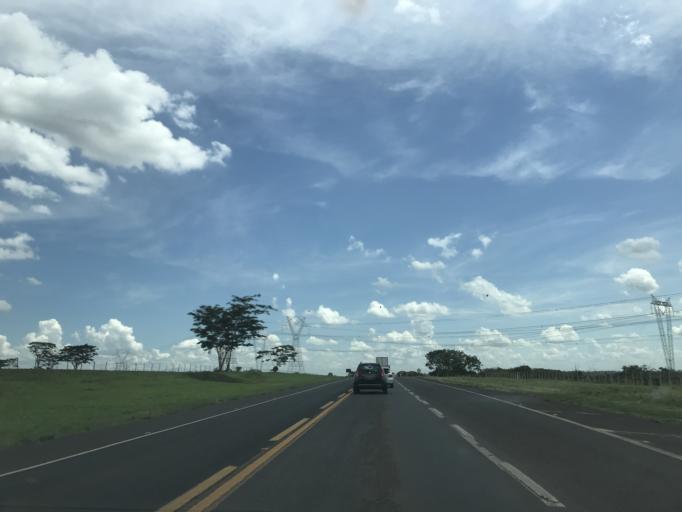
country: BR
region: Sao Paulo
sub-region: Nova Granada
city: Nova Granada
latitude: -20.3326
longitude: -49.2134
